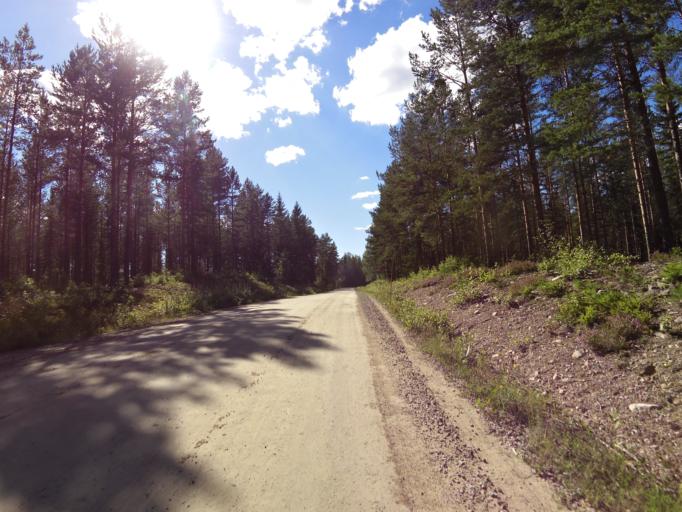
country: SE
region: Dalarna
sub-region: Faluns Kommun
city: Svardsjo
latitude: 60.6403
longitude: 15.8799
